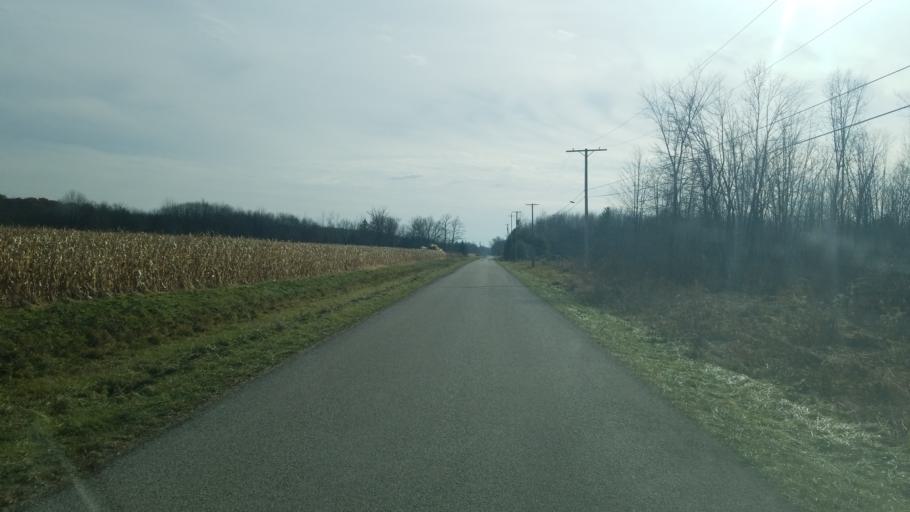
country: US
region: Ohio
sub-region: Ashtabula County
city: Roaming Shores
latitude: 41.6841
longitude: -80.9310
